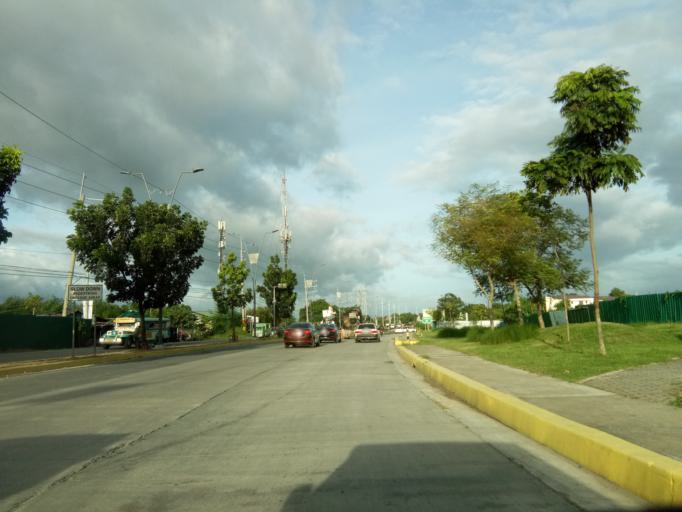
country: PH
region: Calabarzon
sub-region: Province of Cavite
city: Imus
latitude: 14.3862
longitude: 120.9609
